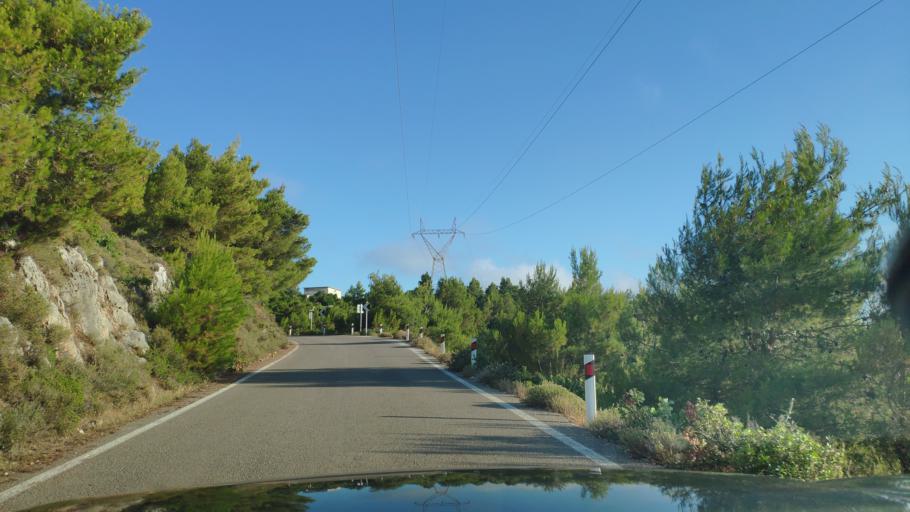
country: GR
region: Ionian Islands
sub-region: Lefkada
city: Nidri
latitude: 38.6215
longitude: 20.5643
